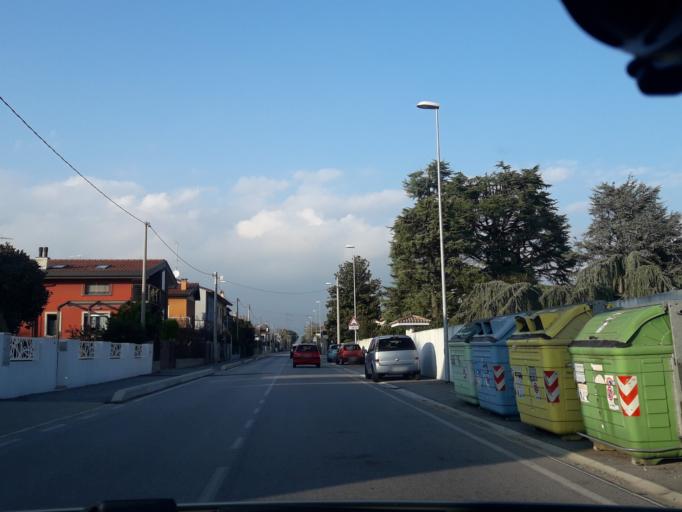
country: IT
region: Friuli Venezia Giulia
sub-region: Provincia di Udine
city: Feletto Umberto
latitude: 46.0894
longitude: 13.2431
